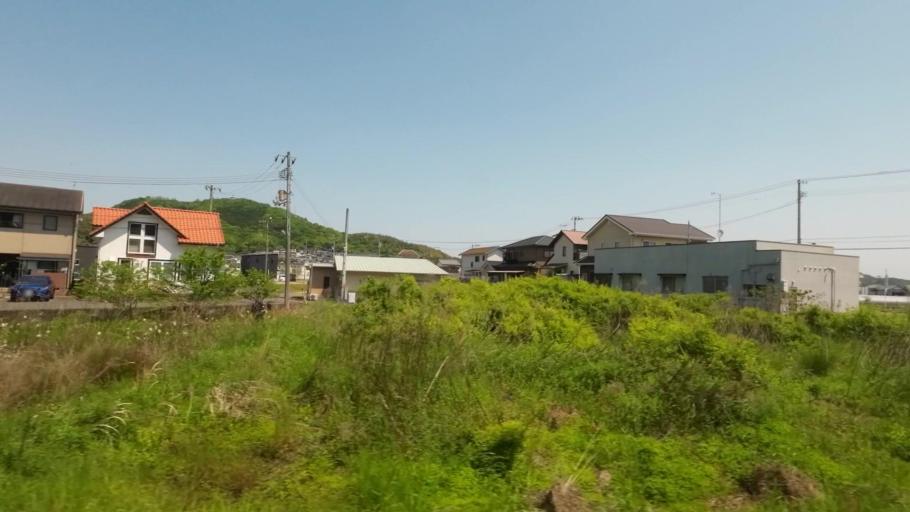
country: JP
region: Ehime
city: Hojo
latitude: 34.0961
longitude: 132.9547
